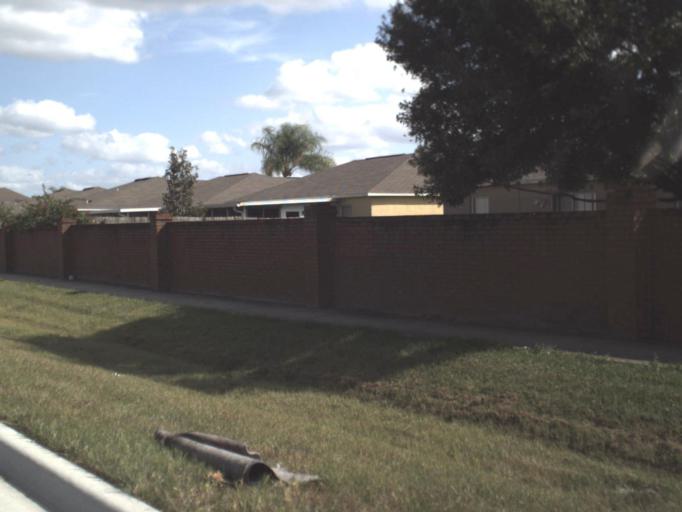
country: US
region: Florida
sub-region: Osceola County
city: Buenaventura Lakes
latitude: 28.3470
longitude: -81.3417
